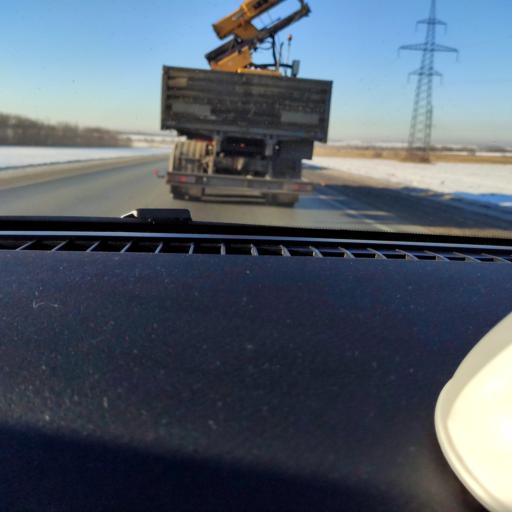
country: RU
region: Samara
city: Smyshlyayevka
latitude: 53.1451
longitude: 50.4622
